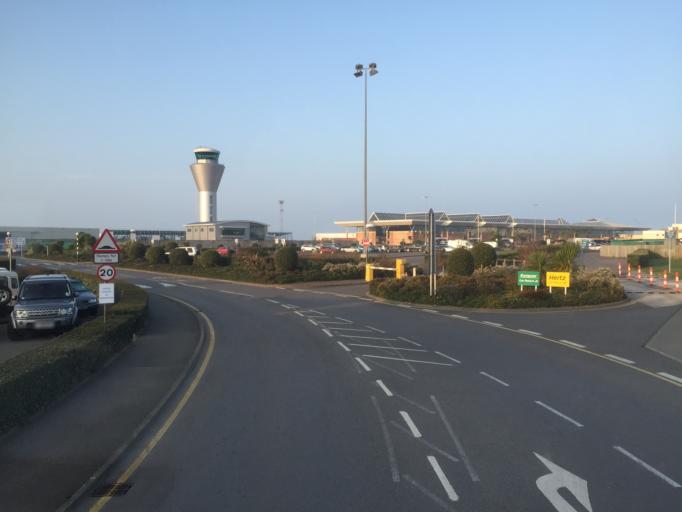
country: JE
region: St Helier
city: Saint Helier
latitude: 49.2061
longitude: -2.1910
